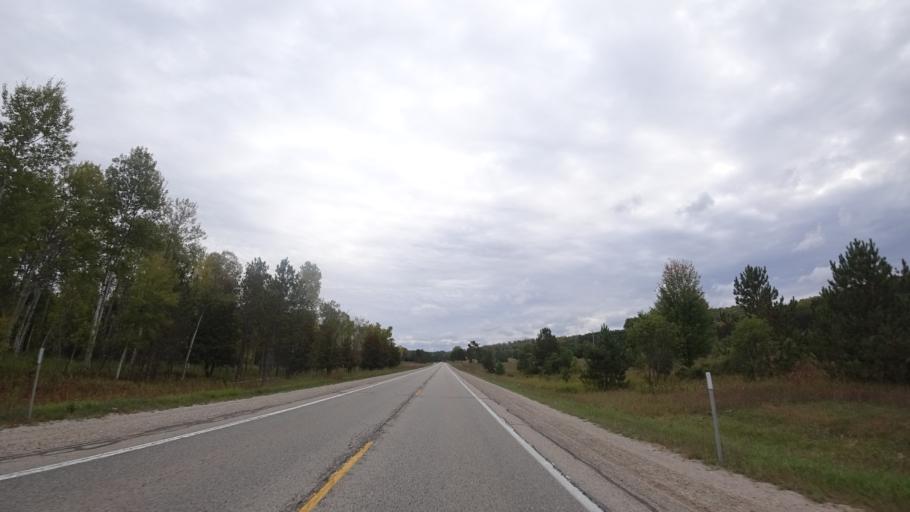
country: US
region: Michigan
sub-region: Charlevoix County
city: Boyne City
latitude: 45.2103
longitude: -84.9253
